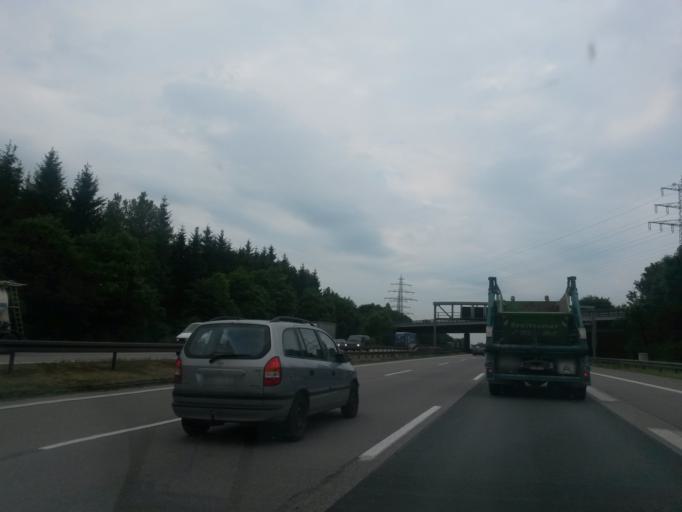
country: DE
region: Bavaria
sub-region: Upper Bavaria
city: Putzbrunn
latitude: 48.0627
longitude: 11.7088
